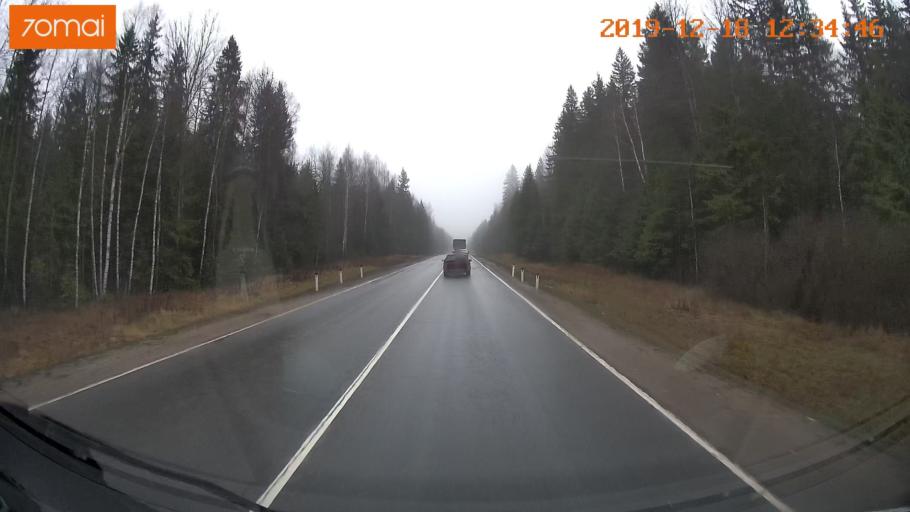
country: RU
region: Moskovskaya
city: Rumyantsevo
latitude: 56.1238
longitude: 36.5757
